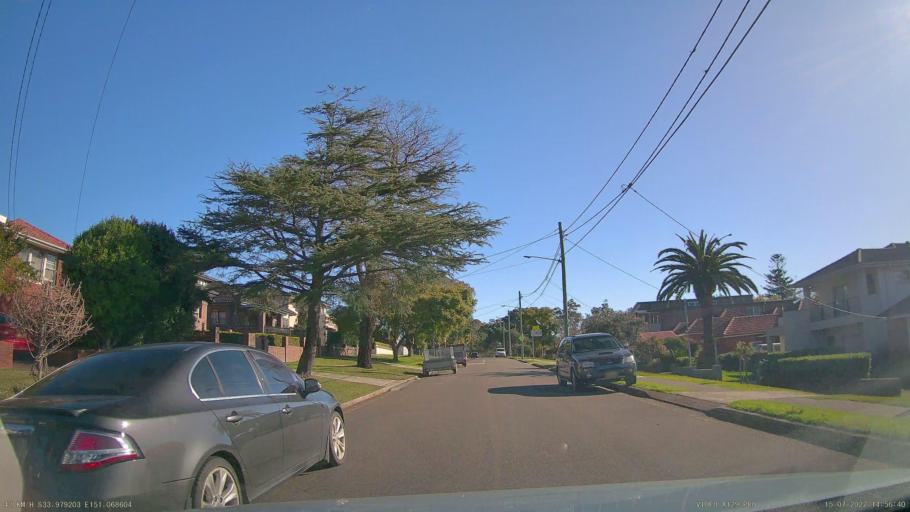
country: AU
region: New South Wales
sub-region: Hurstville
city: Oatley
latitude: -33.9792
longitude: 151.0683
